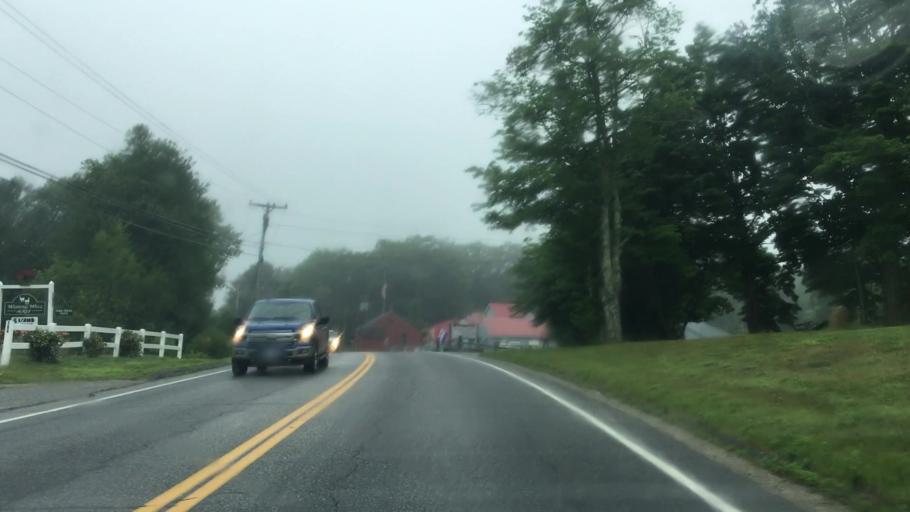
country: US
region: Maine
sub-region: Lincoln County
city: Edgecomb
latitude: 43.9580
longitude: -69.6305
